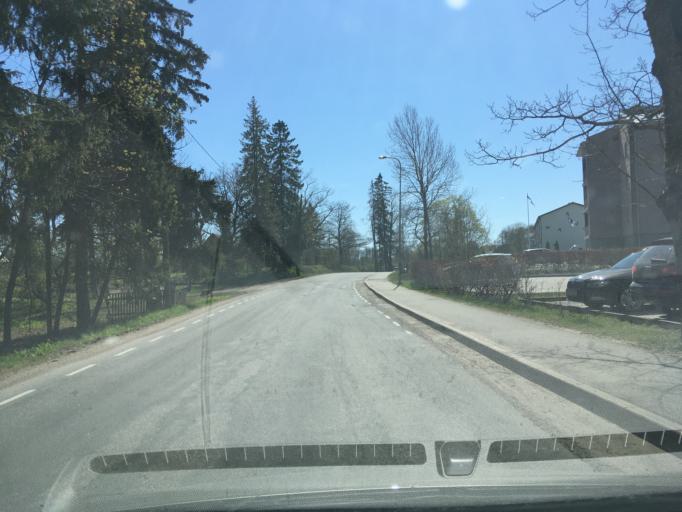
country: EE
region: Harju
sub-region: Raasiku vald
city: Arukula
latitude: 59.3647
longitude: 25.0825
